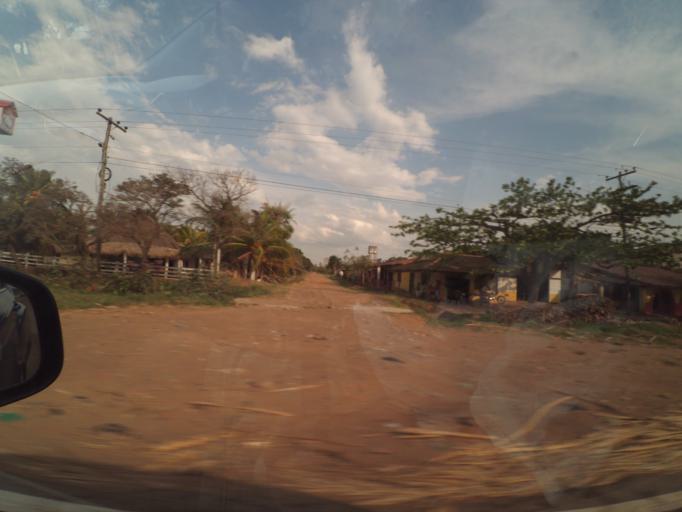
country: BO
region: Santa Cruz
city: Montero
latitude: -17.2650
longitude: -63.0701
